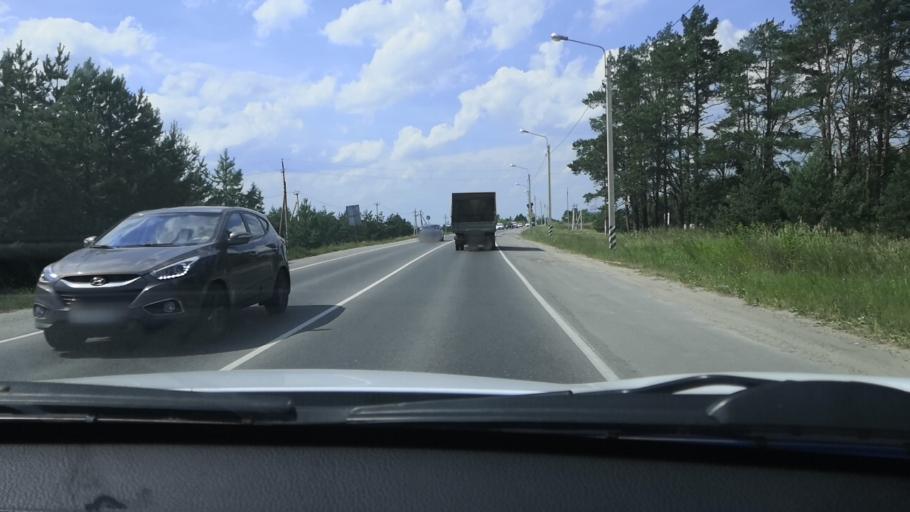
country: RU
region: Rjazan
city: Murmino
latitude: 54.6311
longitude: 39.9525
